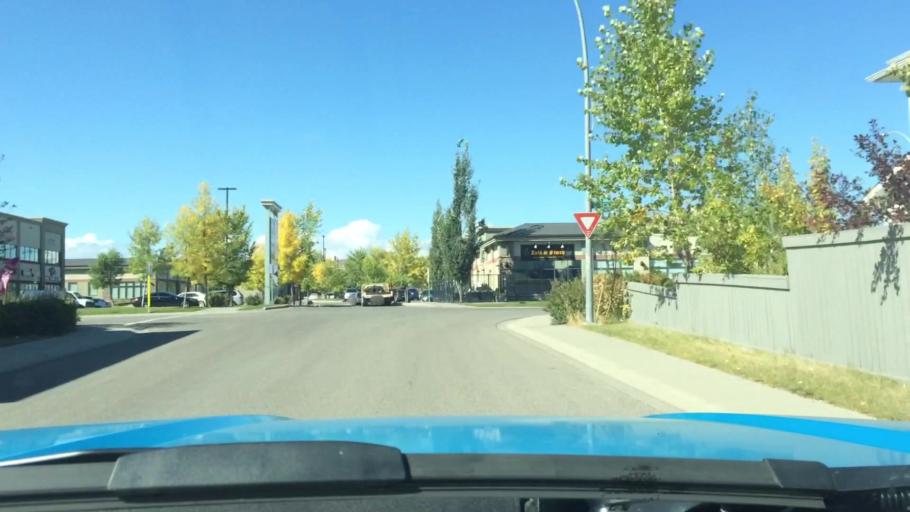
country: CA
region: Alberta
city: Calgary
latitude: 50.9057
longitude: -114.1098
